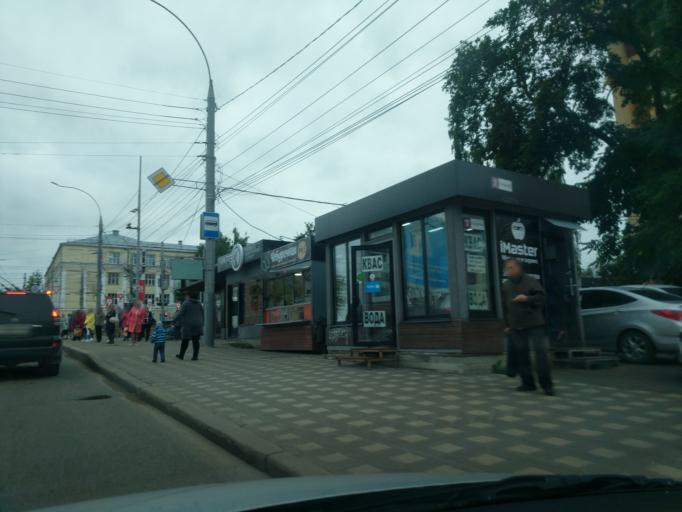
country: RU
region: Kirov
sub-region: Kirovo-Chepetskiy Rayon
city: Kirov
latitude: 58.5946
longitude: 49.6686
